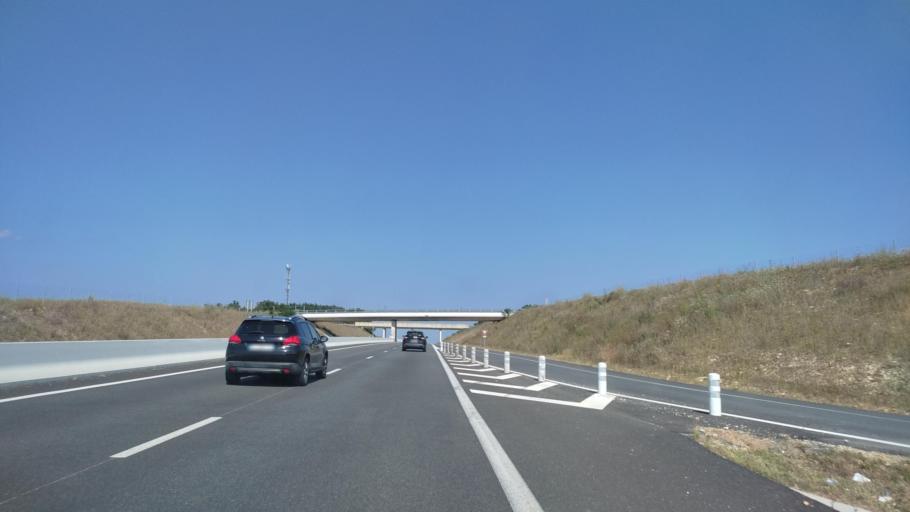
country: FR
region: Poitou-Charentes
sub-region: Departement de la Charente
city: Saint-Saturnin
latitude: 45.6817
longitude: 0.0698
